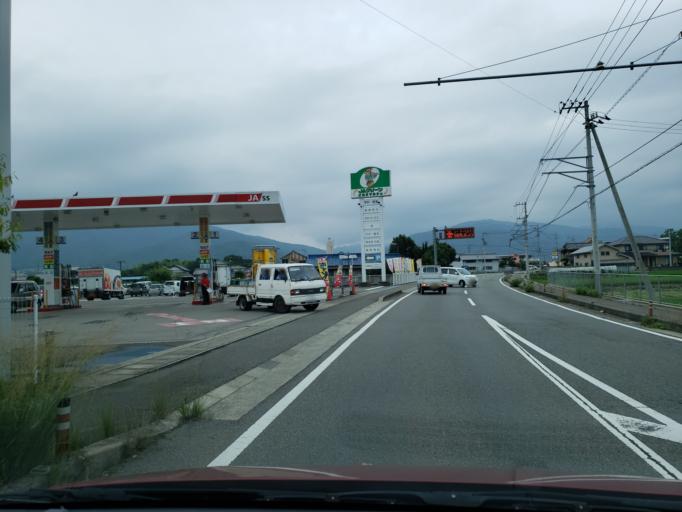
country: JP
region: Tokushima
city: Kamojimacho-jogejima
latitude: 34.1031
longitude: 134.3453
